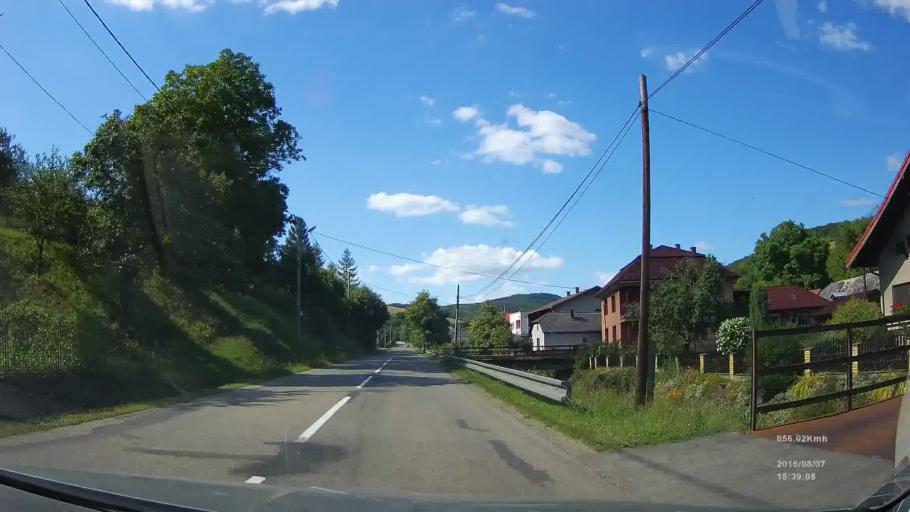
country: SK
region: Presovsky
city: Giraltovce
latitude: 49.1156
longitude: 21.6060
